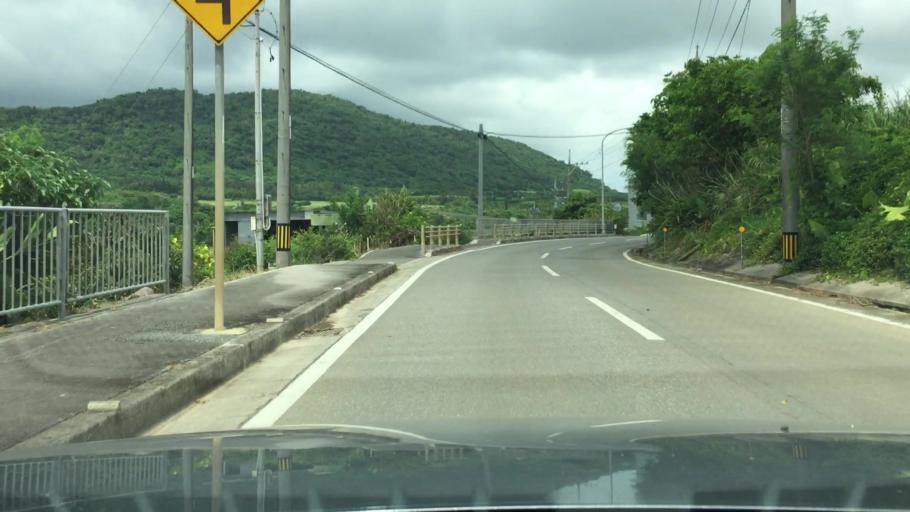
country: JP
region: Okinawa
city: Ishigaki
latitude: 24.3936
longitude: 124.1676
